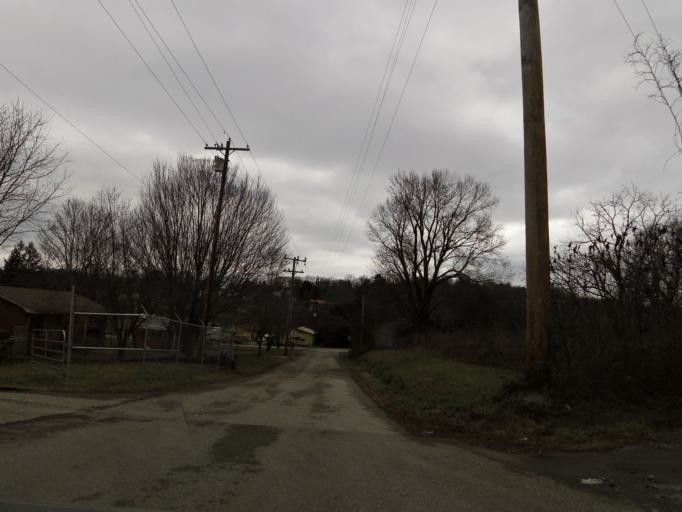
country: US
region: Tennessee
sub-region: Jefferson County
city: Jefferson City
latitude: 36.1252
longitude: -83.4963
